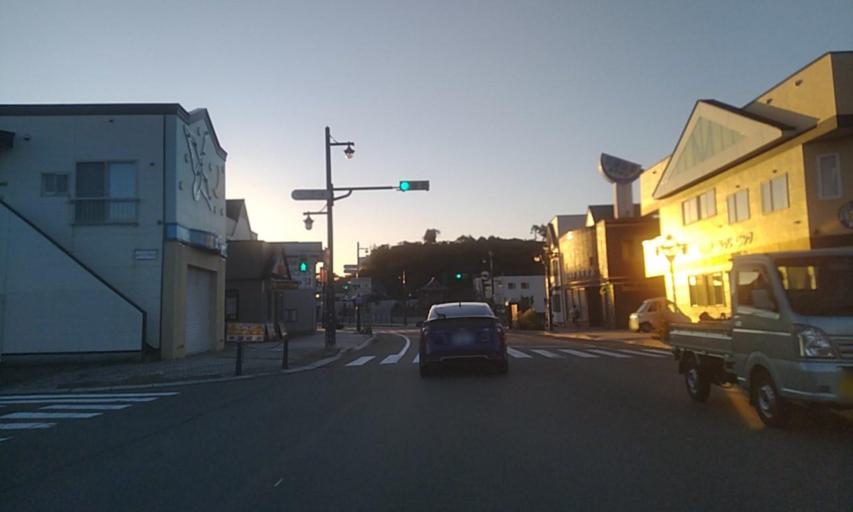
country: JP
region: Hokkaido
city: Shizunai-furukawacho
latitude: 42.1607
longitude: 142.7797
